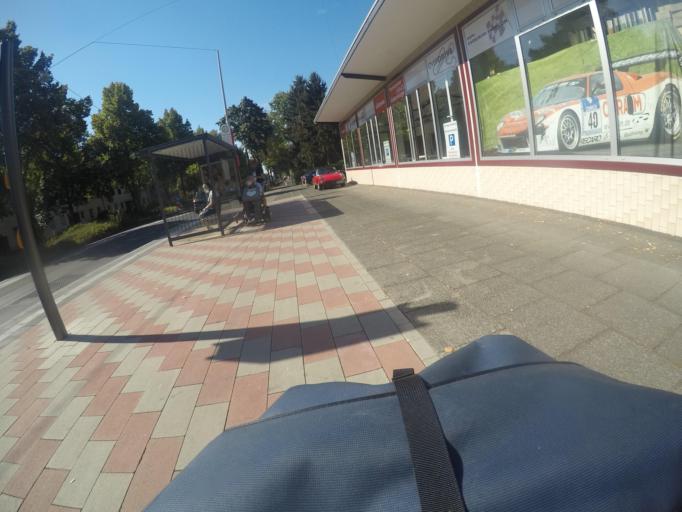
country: DE
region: North Rhine-Westphalia
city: Opladen
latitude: 51.0583
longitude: 7.0028
